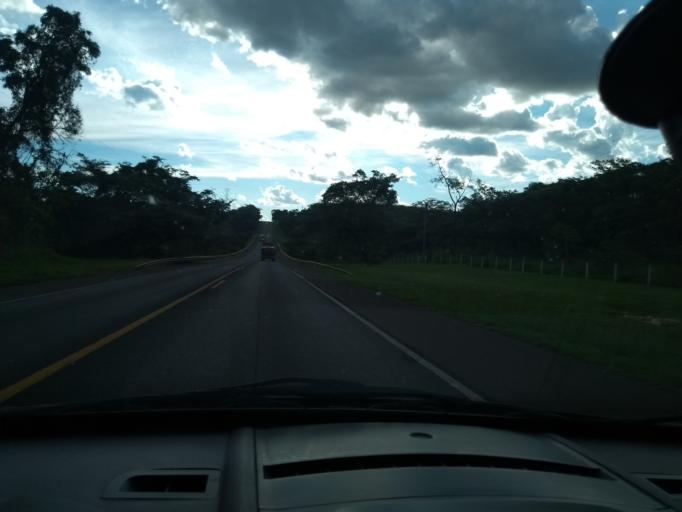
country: BR
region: Sao Paulo
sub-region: Casa Branca
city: Casa Branca
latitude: -21.7987
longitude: -47.0854
